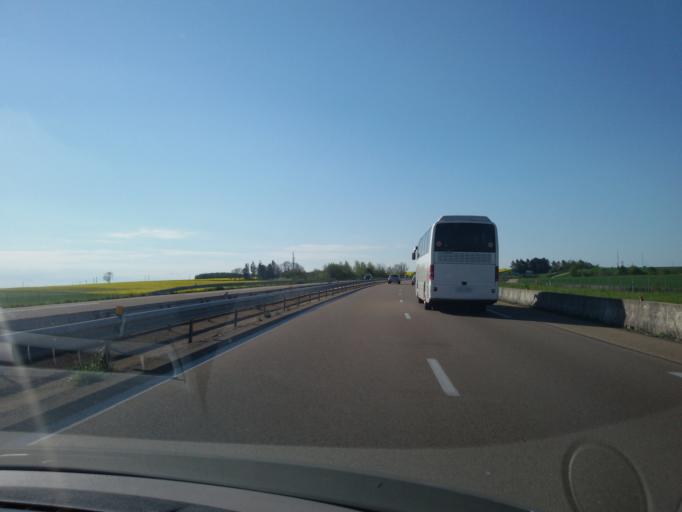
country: FR
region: Bourgogne
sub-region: Departement de l'Yonne
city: Saint-Bris-le-Vineux
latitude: 47.7655
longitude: 3.7287
